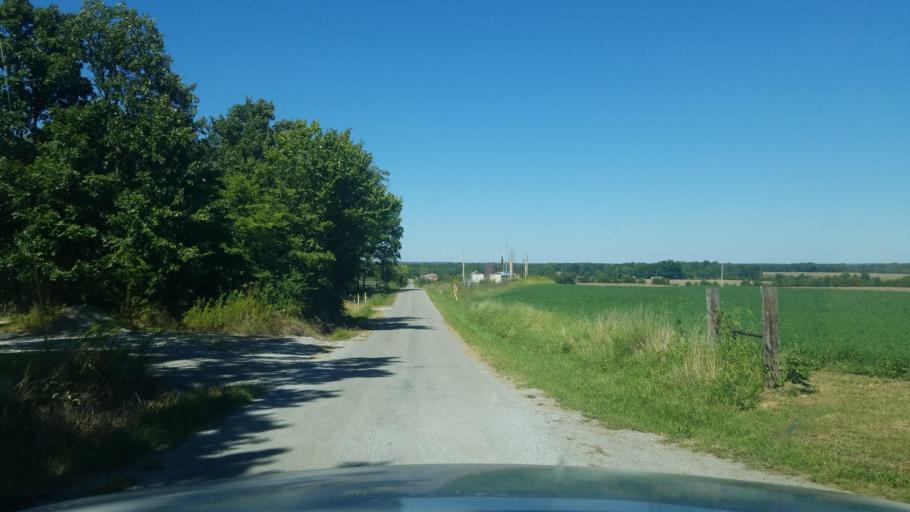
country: US
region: Illinois
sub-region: Saline County
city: Eldorado
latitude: 37.8546
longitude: -88.5119
